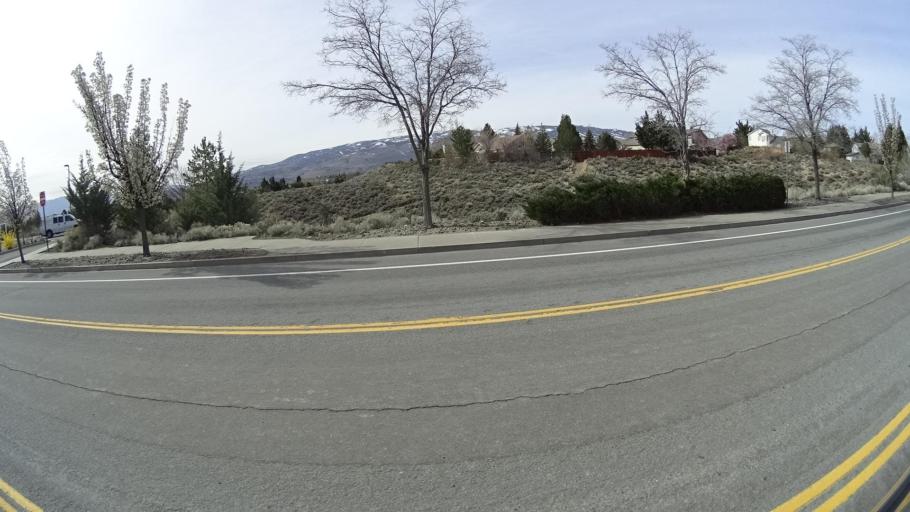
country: US
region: Nevada
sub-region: Washoe County
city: Reno
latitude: 39.5427
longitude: -119.8696
